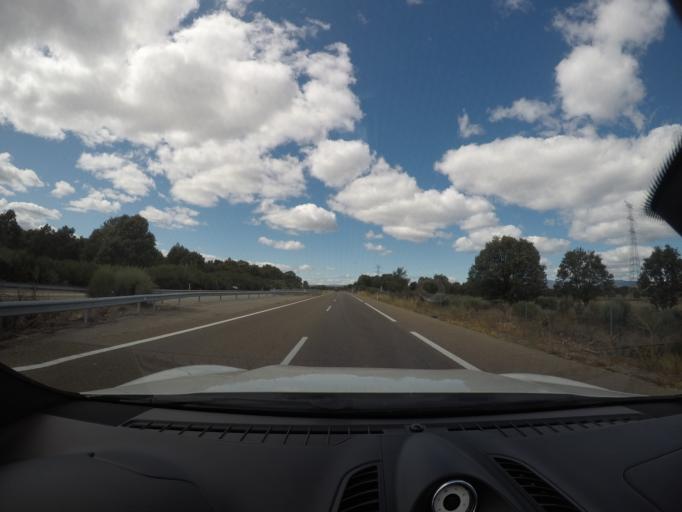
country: ES
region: Castille and Leon
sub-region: Provincia de Zamora
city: Cernadilla
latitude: 42.0264
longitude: -6.4067
